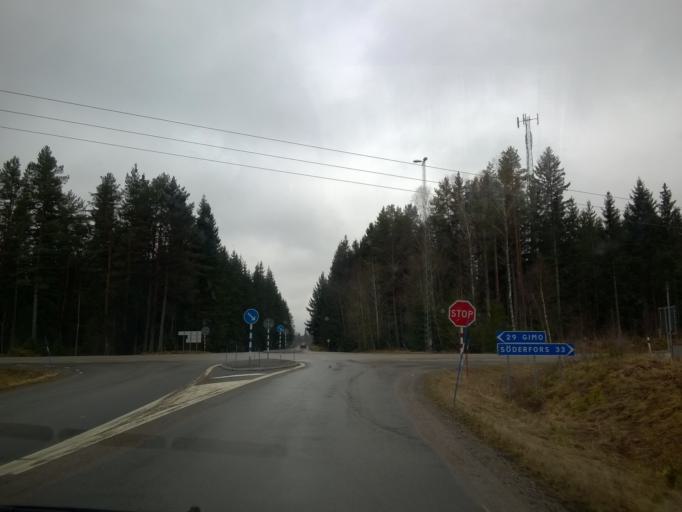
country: SE
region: Uppsala
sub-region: Tierps Kommun
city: Orbyhus
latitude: 60.2170
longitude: 17.7027
